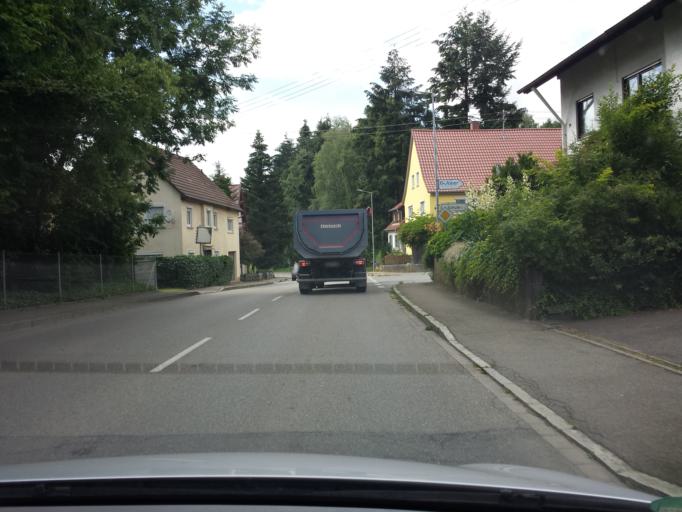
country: DE
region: Baden-Wuerttemberg
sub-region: Tuebingen Region
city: Burgrieden
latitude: 48.2373
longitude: 9.9364
